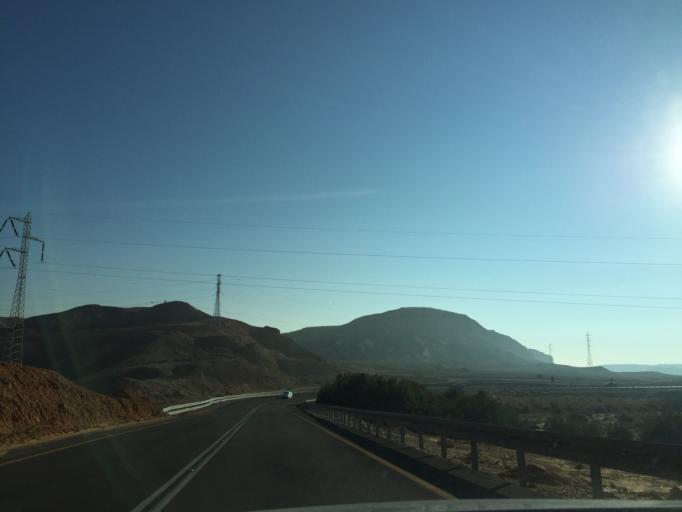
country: IL
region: Southern District
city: Mitzpe Ramon
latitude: 30.3204
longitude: 34.9648
